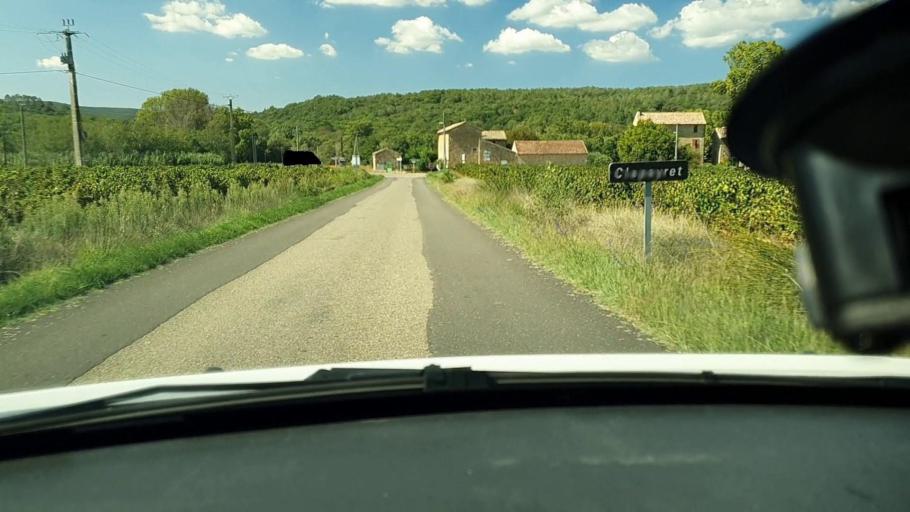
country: FR
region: Languedoc-Roussillon
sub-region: Departement du Gard
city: Goudargues
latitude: 44.1835
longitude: 4.4788
